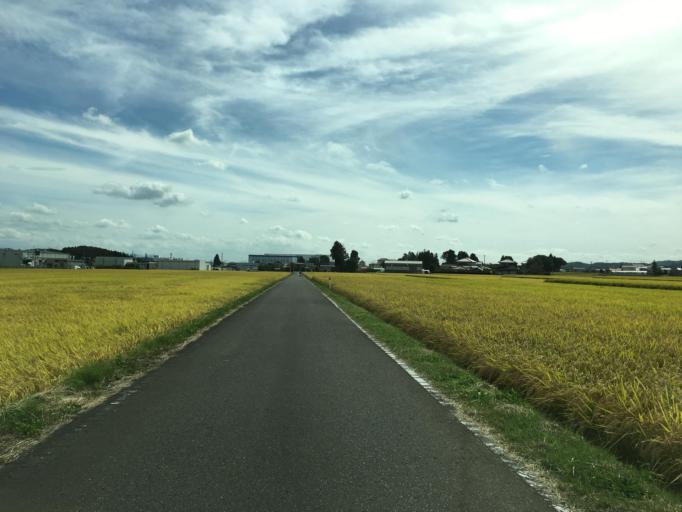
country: JP
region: Fukushima
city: Motomiya
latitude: 37.5378
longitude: 140.3948
